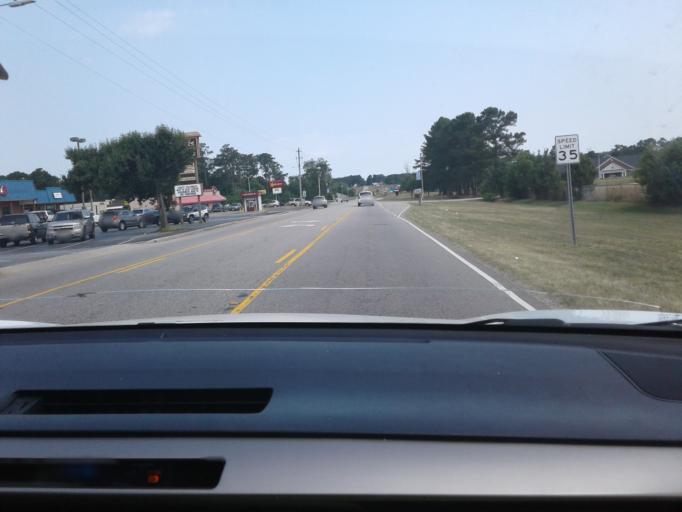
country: US
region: North Carolina
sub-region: Harnett County
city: Coats
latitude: 35.4132
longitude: -78.6729
